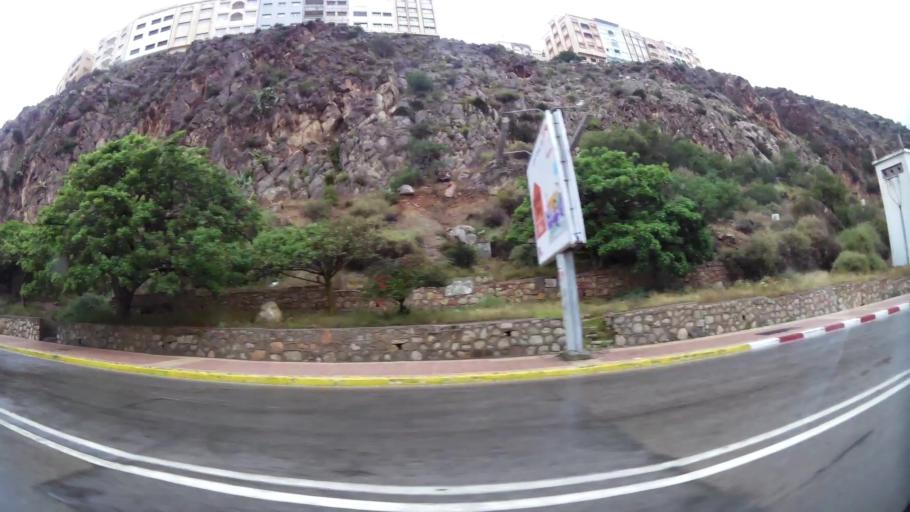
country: MA
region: Taza-Al Hoceima-Taounate
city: Al Hoceima
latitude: 35.2488
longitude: -3.9262
